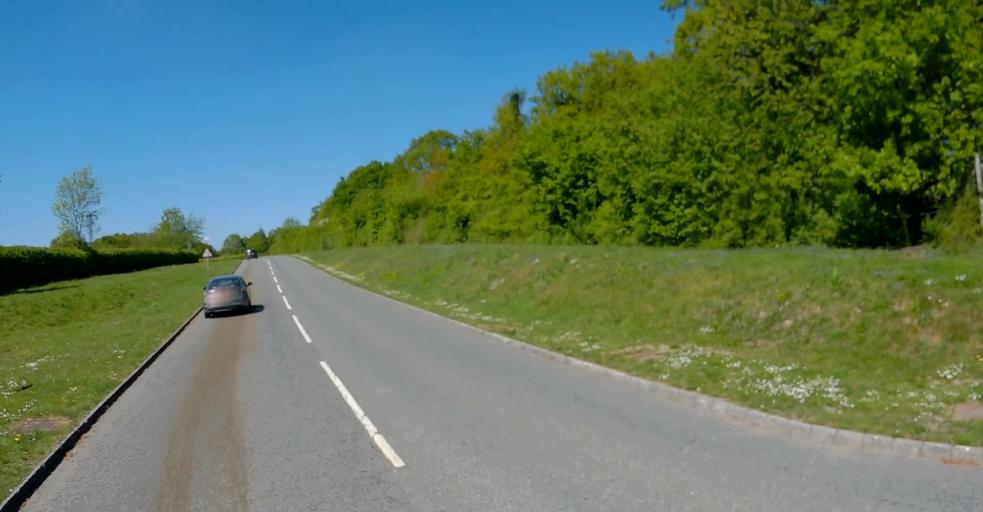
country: GB
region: England
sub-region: Hampshire
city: Andover
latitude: 51.1877
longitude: -1.4057
